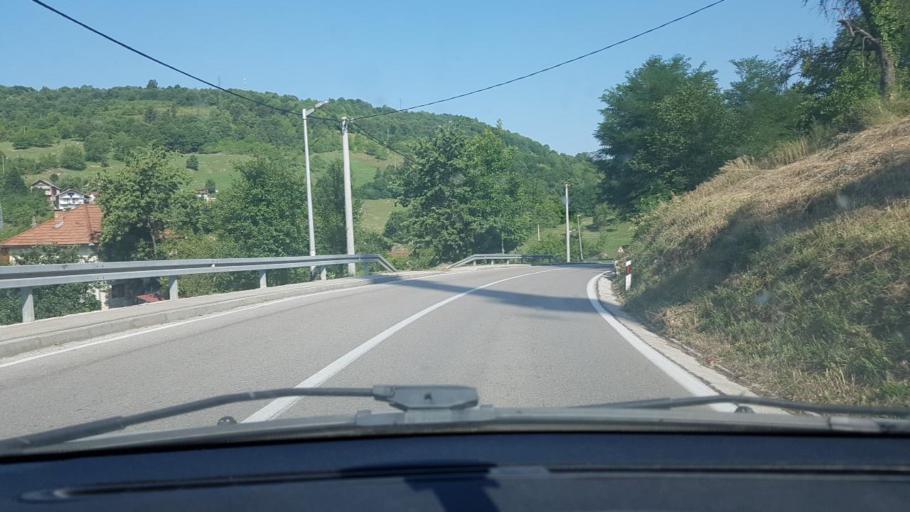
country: BA
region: Federation of Bosnia and Herzegovina
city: Pecigrad
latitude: 45.0551
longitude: 15.8959
